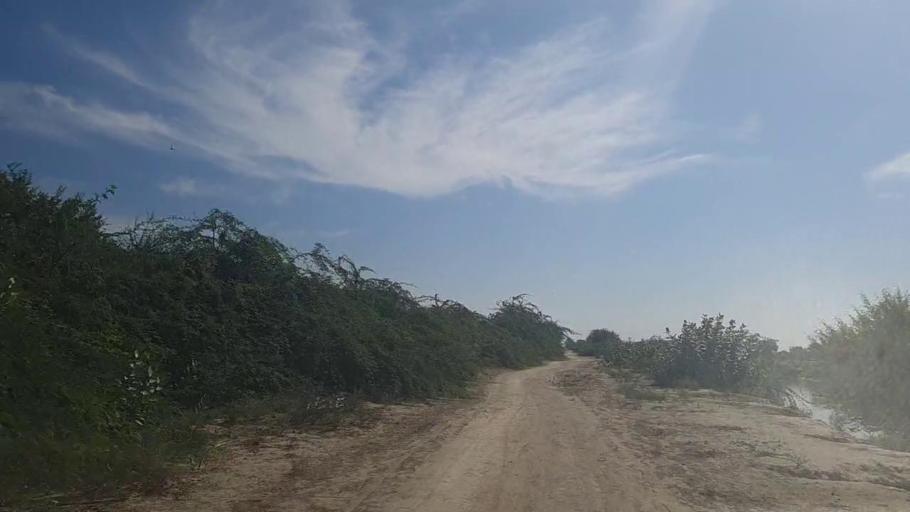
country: PK
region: Sindh
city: Mirpur Batoro
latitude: 24.6568
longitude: 68.1985
